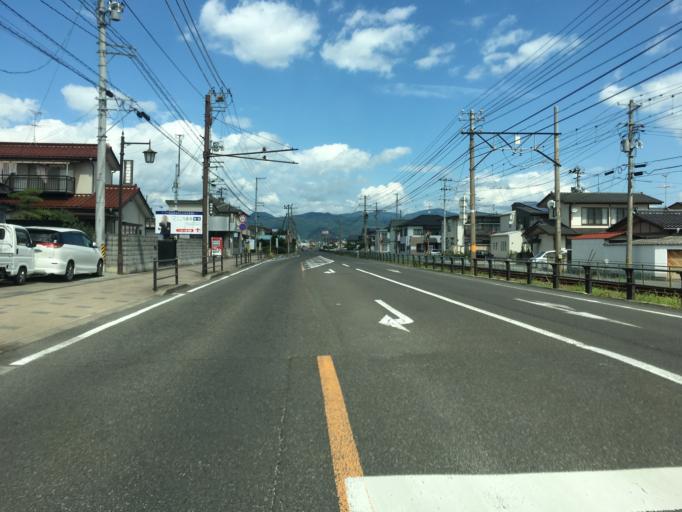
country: JP
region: Fukushima
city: Fukushima-shi
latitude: 37.7902
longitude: 140.4400
